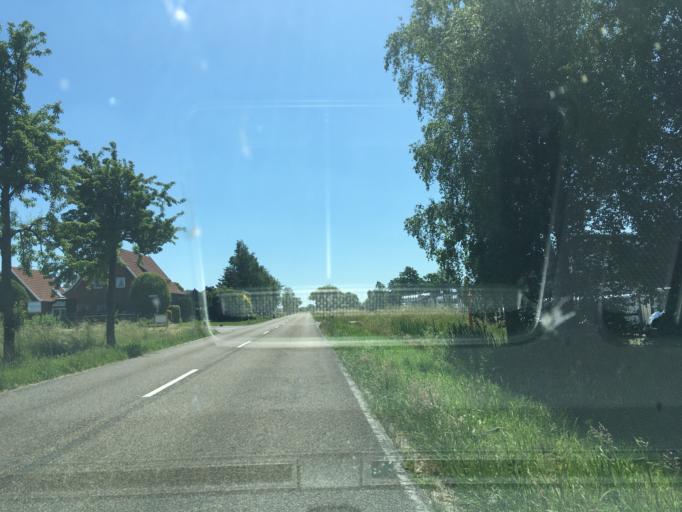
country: DE
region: North Rhine-Westphalia
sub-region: Regierungsbezirk Munster
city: Raesfeld
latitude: 51.7859
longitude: 6.8194
